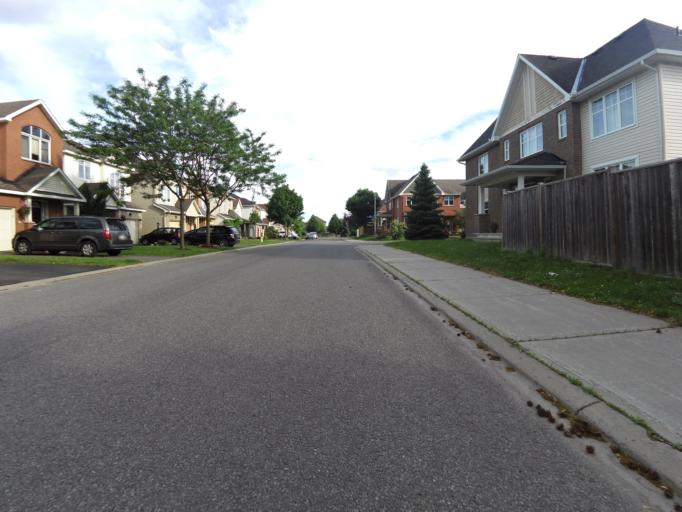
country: CA
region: Ontario
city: Ottawa
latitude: 45.2875
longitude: -75.7069
